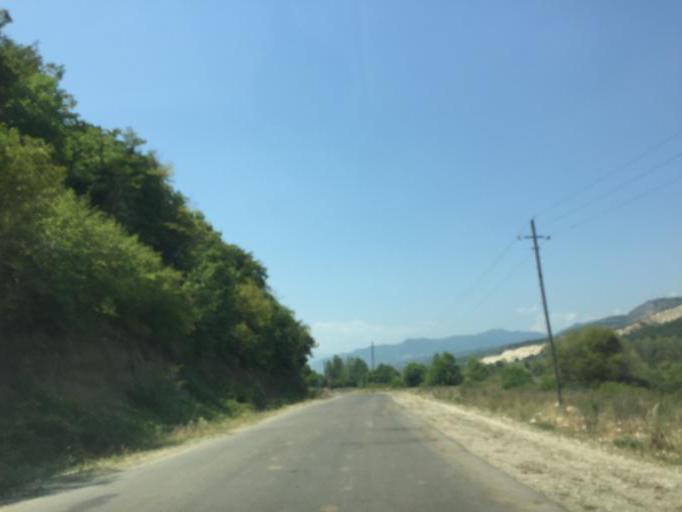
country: AZ
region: Tartar Rayon
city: Martakert
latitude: 40.1409
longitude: 46.5542
